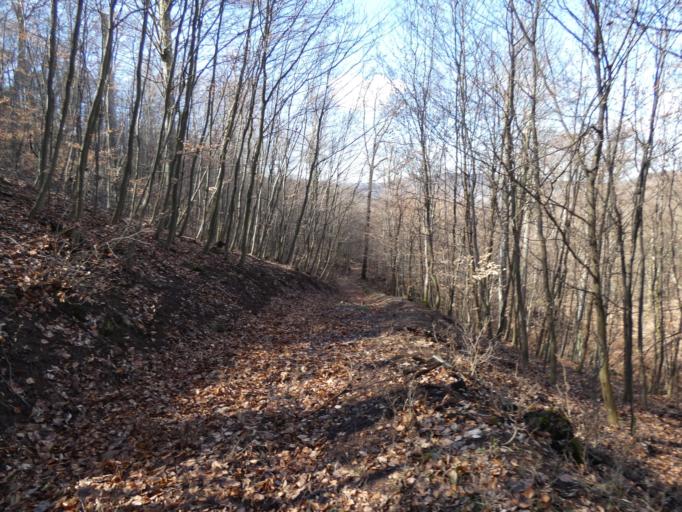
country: HU
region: Pest
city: Visegrad
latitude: 47.7641
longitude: 19.0034
